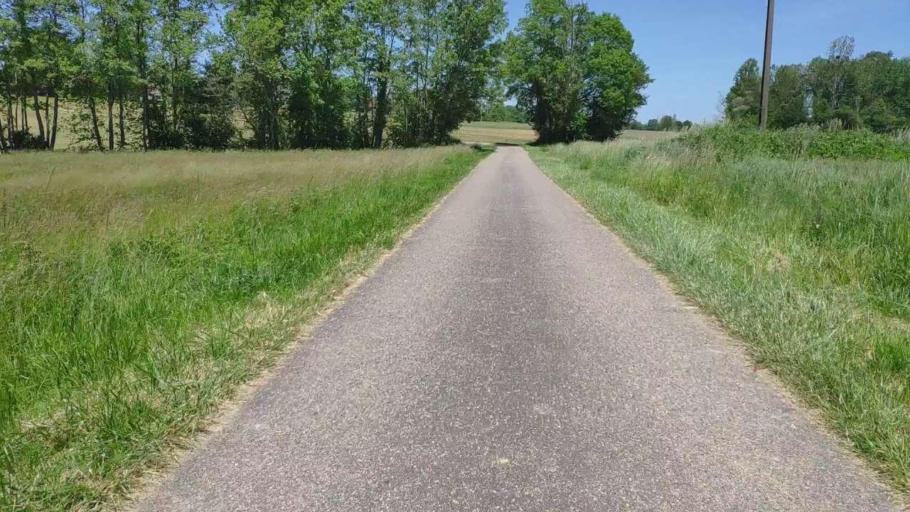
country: FR
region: Franche-Comte
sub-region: Departement du Jura
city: Bletterans
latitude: 46.7966
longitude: 5.3888
